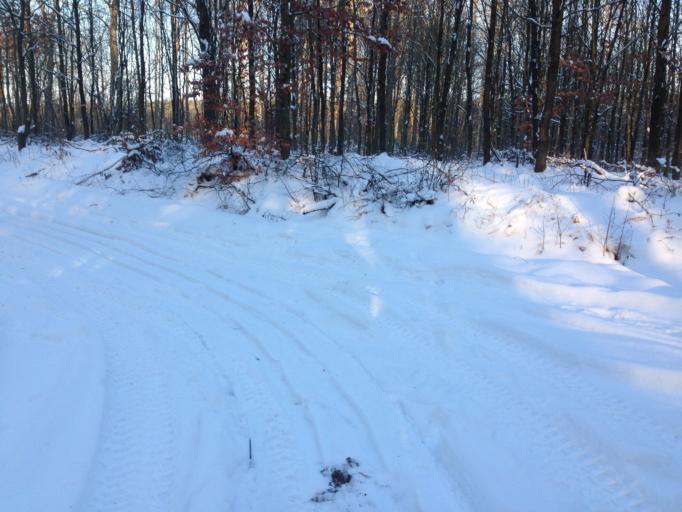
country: PL
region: Kujawsko-Pomorskie
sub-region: Powiat brodnicki
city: Gorzno
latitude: 53.1812
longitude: 19.6842
